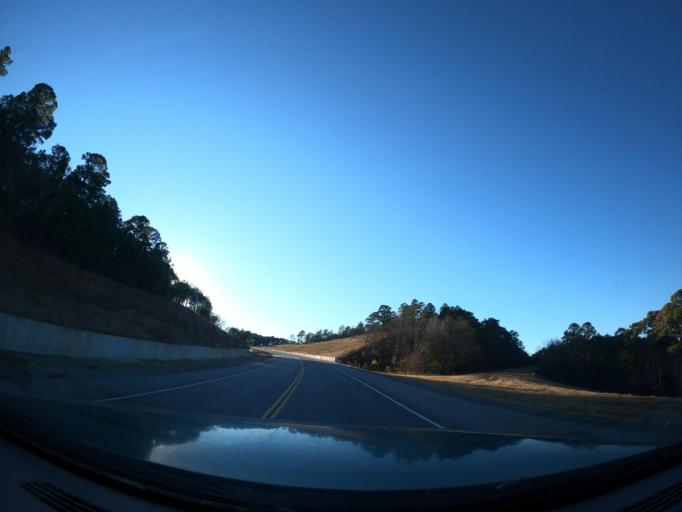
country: US
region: Oklahoma
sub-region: Pittsburg County
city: Hartshorne
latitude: 34.8912
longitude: -95.4548
